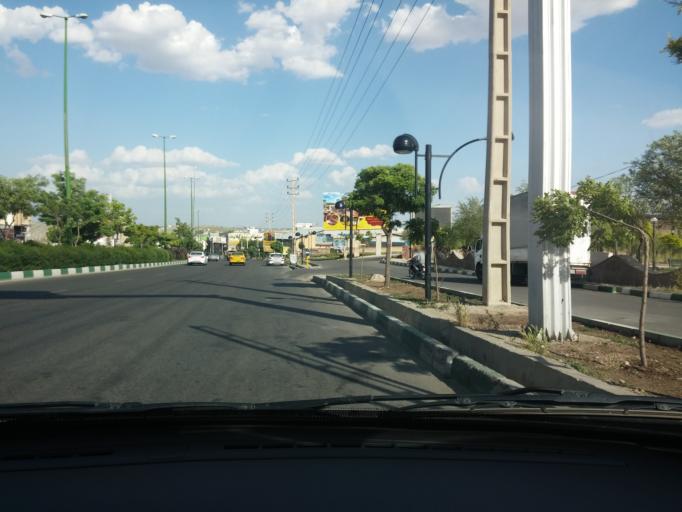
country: IR
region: Tehran
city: Damavand
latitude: 35.6870
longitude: 52.0144
